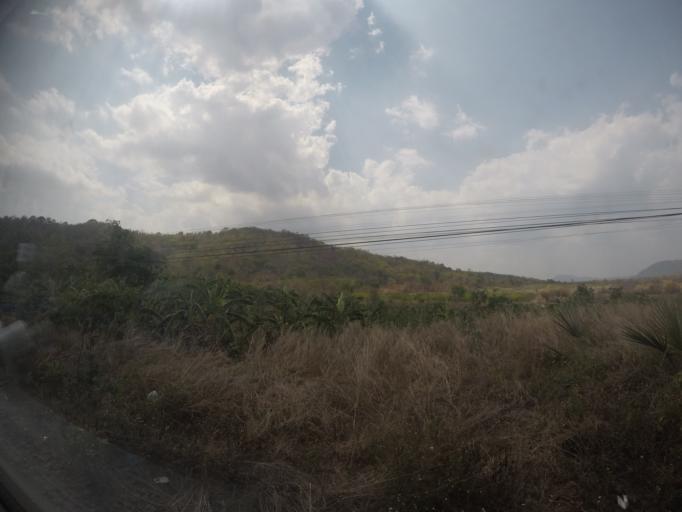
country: VN
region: Binh Thuan
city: Thuan Nam
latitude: 10.8811
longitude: 107.7196
